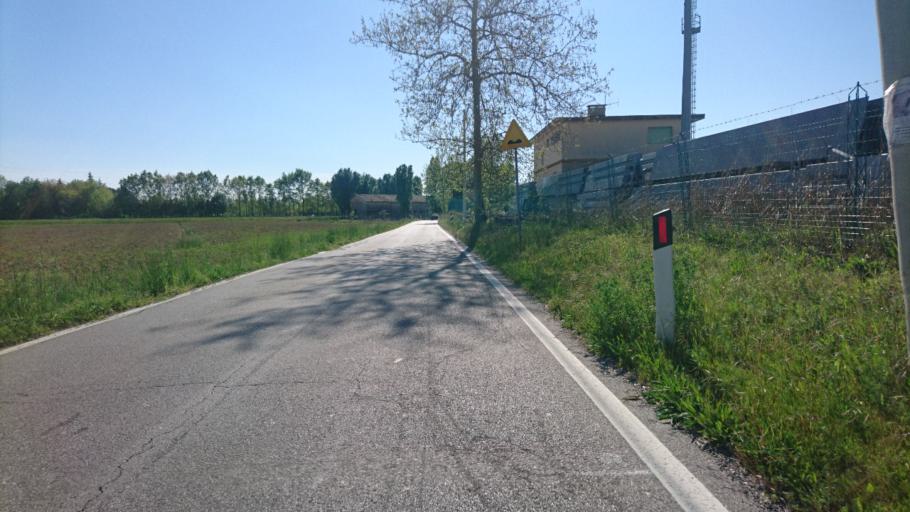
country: IT
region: Veneto
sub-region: Provincia di Venezia
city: Dese
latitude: 45.5310
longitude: 12.2724
